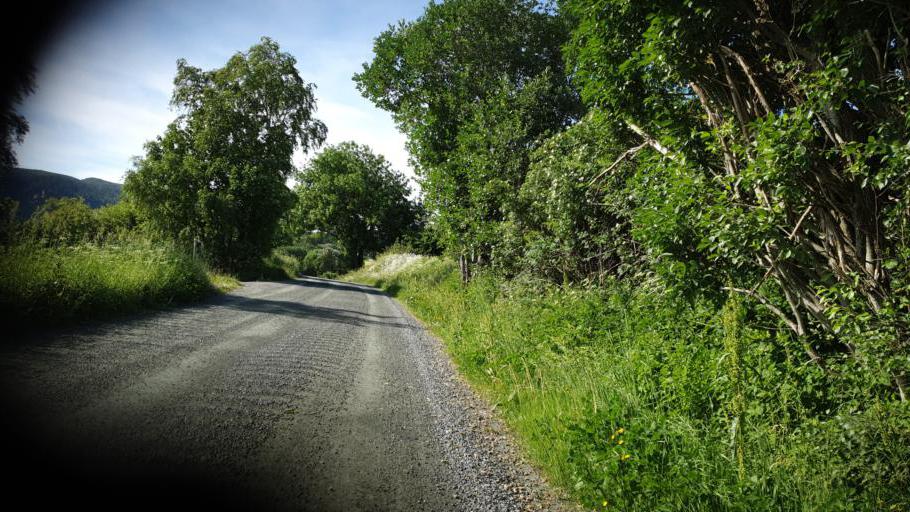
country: NO
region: Sor-Trondelag
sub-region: Trondheim
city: Trondheim
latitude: 63.5715
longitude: 10.4059
